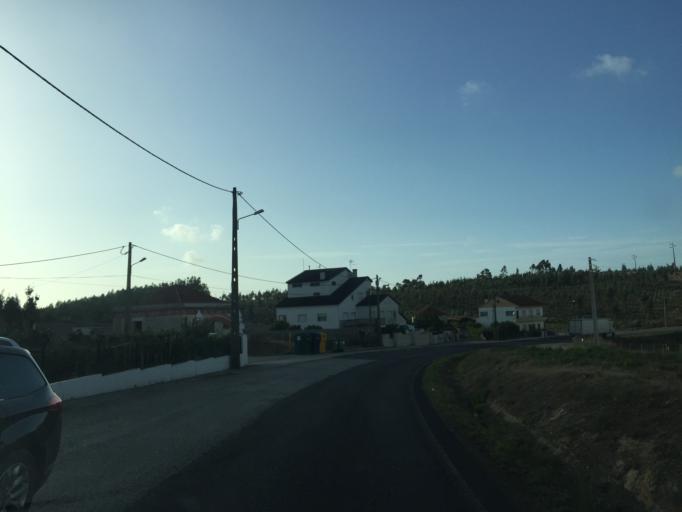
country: PT
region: Lisbon
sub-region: Torres Vedras
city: Torres Vedras
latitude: 39.1174
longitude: -9.2633
